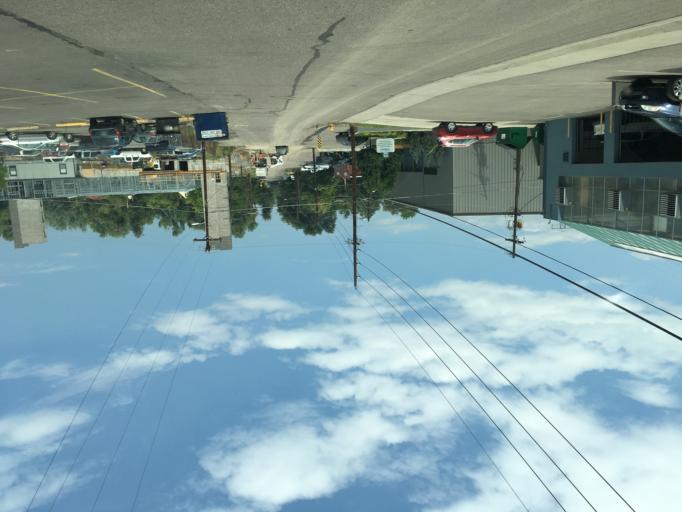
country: US
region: Colorado
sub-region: Jefferson County
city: Wheat Ridge
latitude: 39.7404
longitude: -105.1036
